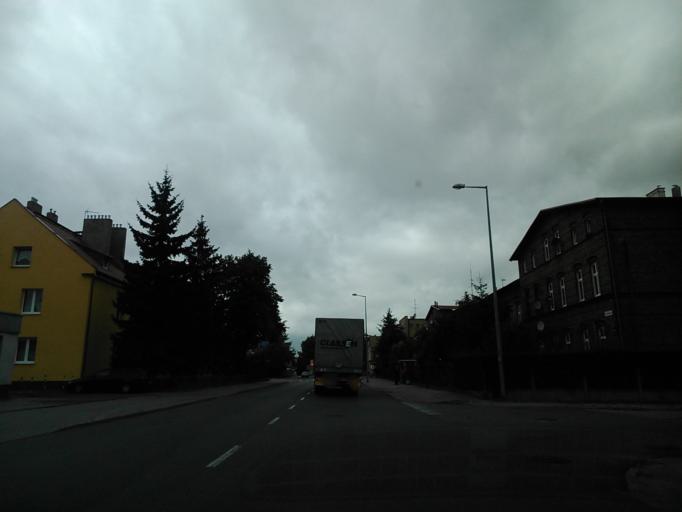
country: PL
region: Kujawsko-Pomorskie
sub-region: Powiat inowroclawski
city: Kruszwica
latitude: 52.6774
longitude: 18.3173
